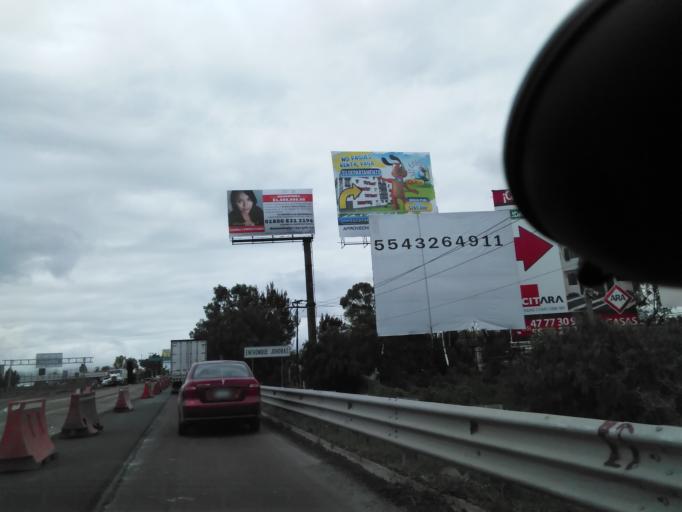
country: MX
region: Mexico
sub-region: Huehuetoca
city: Jorobas
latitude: 19.8237
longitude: -99.2466
